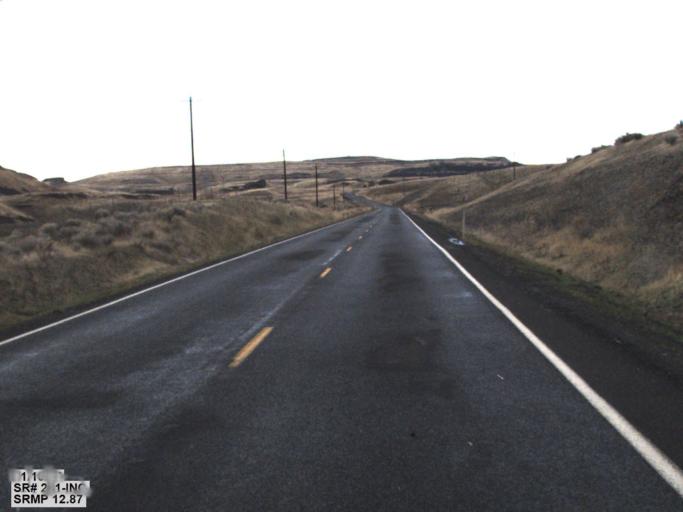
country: US
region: Washington
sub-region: Walla Walla County
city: Waitsburg
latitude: 46.5674
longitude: -118.1918
